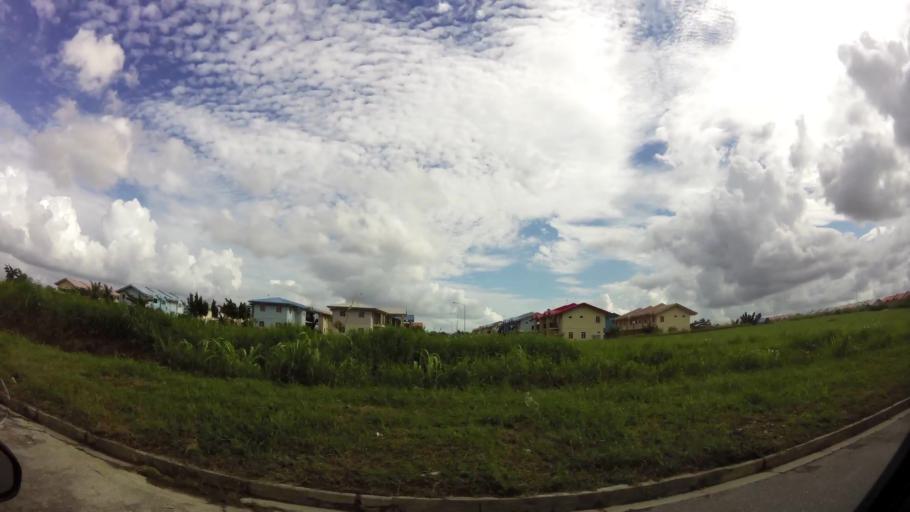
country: TT
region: Chaguanas
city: Chaguanas
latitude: 10.5026
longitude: -61.3950
